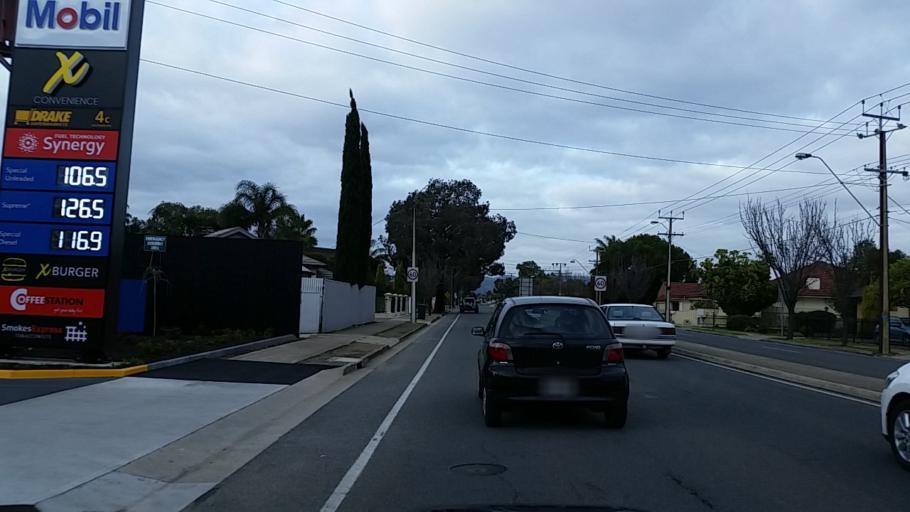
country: AU
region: South Australia
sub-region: Marion
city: South Plympton
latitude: -34.9684
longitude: 138.5490
